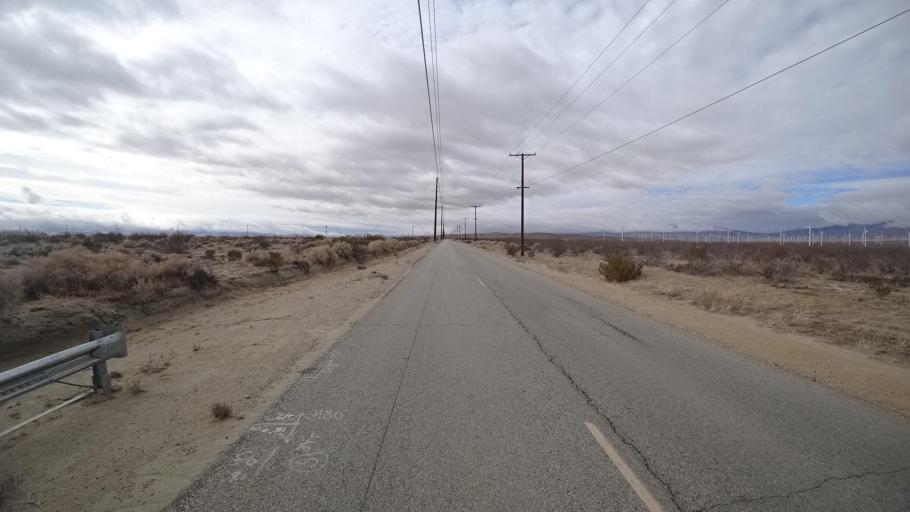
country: US
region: California
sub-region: Kern County
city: Rosamond
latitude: 34.8628
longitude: -118.3939
